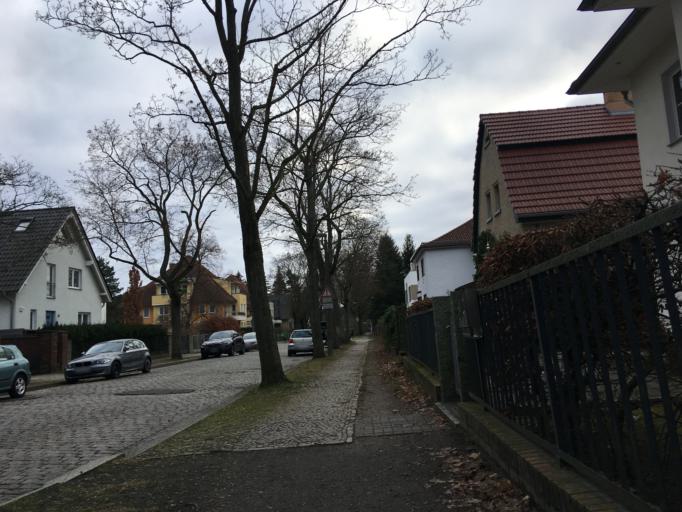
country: DE
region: Berlin
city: Niederschonhausen
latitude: 52.5815
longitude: 13.3888
